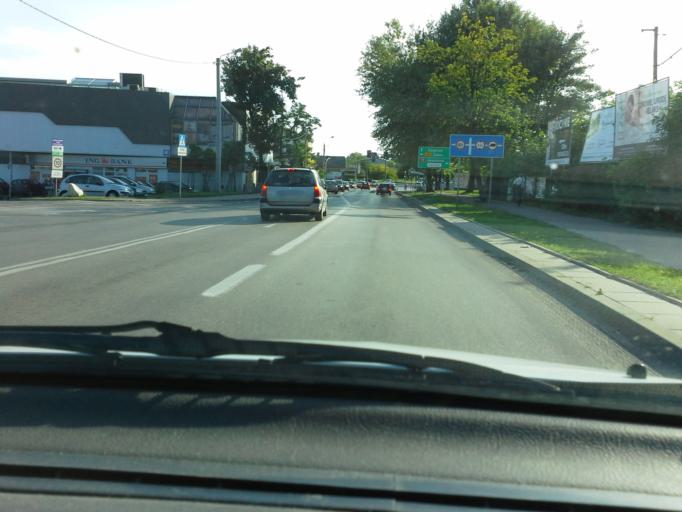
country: PL
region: Lesser Poland Voivodeship
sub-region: Powiat chrzanowski
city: Chrzanow
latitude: 50.1427
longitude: 19.4128
